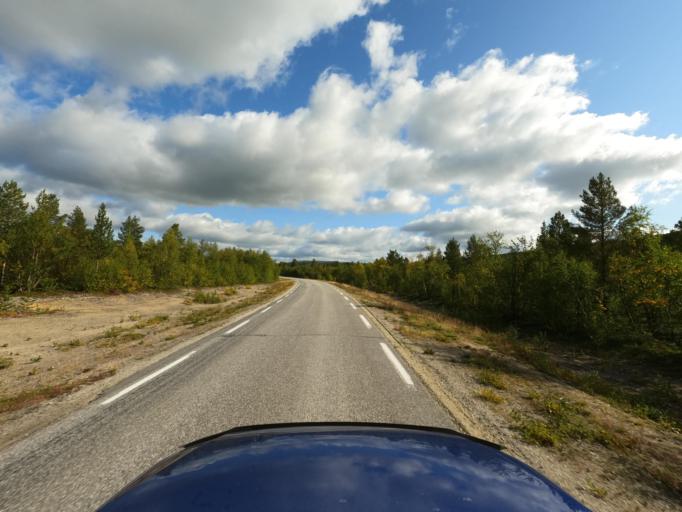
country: NO
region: Finnmark Fylke
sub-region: Karasjok
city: Karasjohka
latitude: 69.4314
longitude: 24.9654
